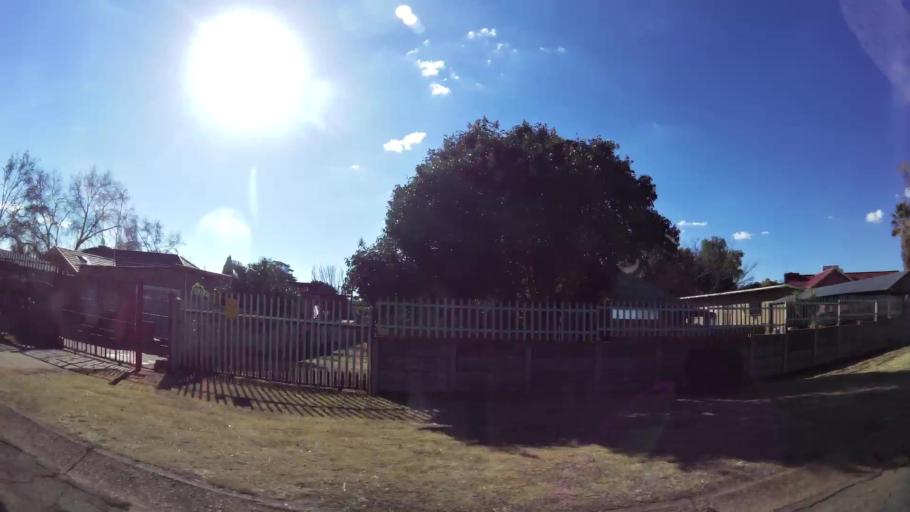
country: ZA
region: Gauteng
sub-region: West Rand District Municipality
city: Carletonville
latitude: -26.3753
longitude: 27.4001
